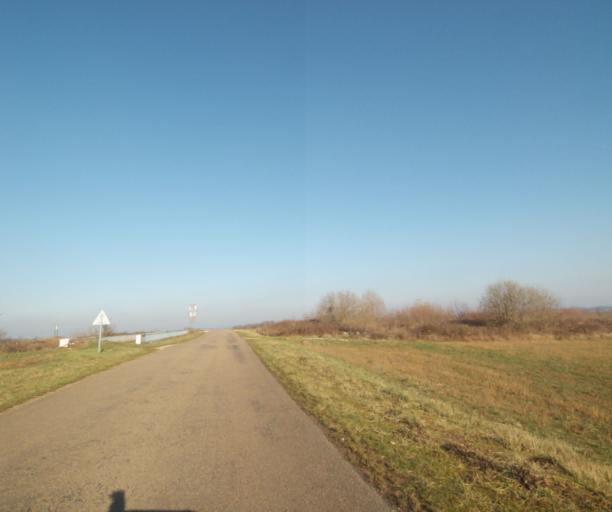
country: FR
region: Champagne-Ardenne
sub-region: Departement de la Haute-Marne
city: Chevillon
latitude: 48.5128
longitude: 5.0872
